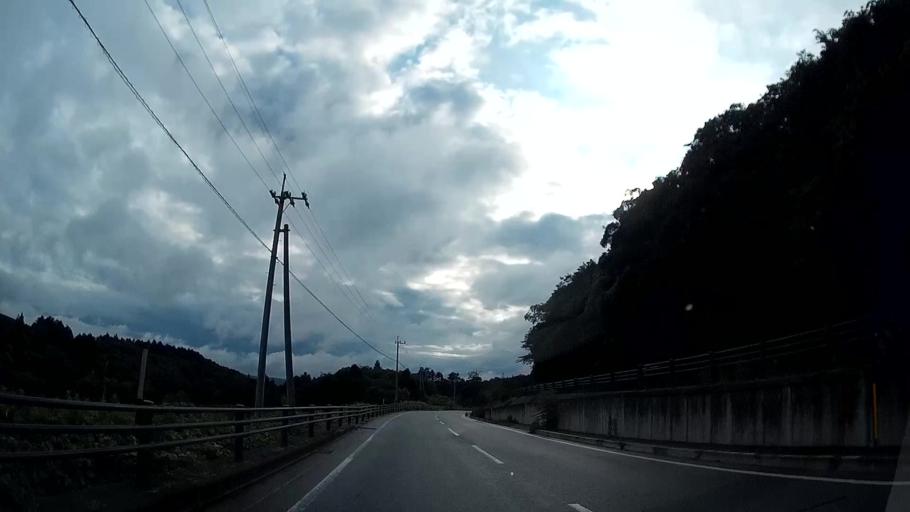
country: JP
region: Kumamoto
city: Ozu
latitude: 32.8760
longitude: 130.9380
